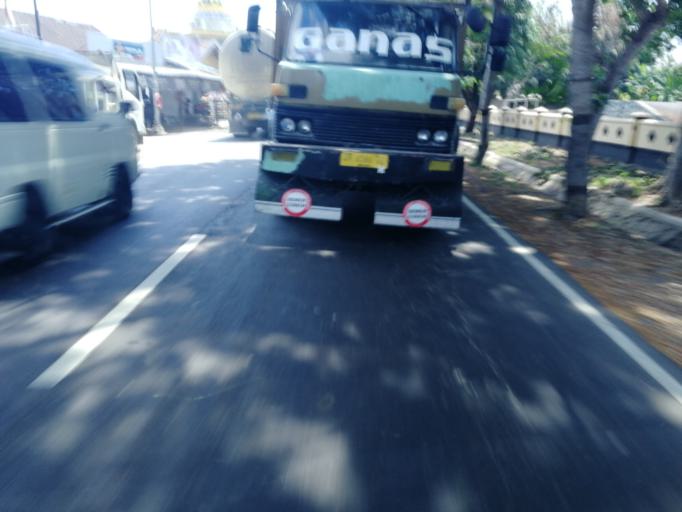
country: ID
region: West Nusa Tenggara
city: Jelateng Timur
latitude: -8.7050
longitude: 116.0880
